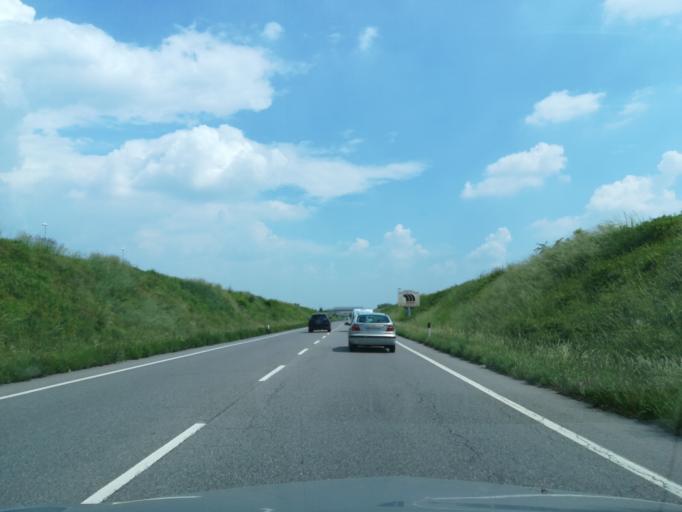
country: IT
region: Lombardy
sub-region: Provincia di Bergamo
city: Brusaporto
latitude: 45.6667
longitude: 9.7580
